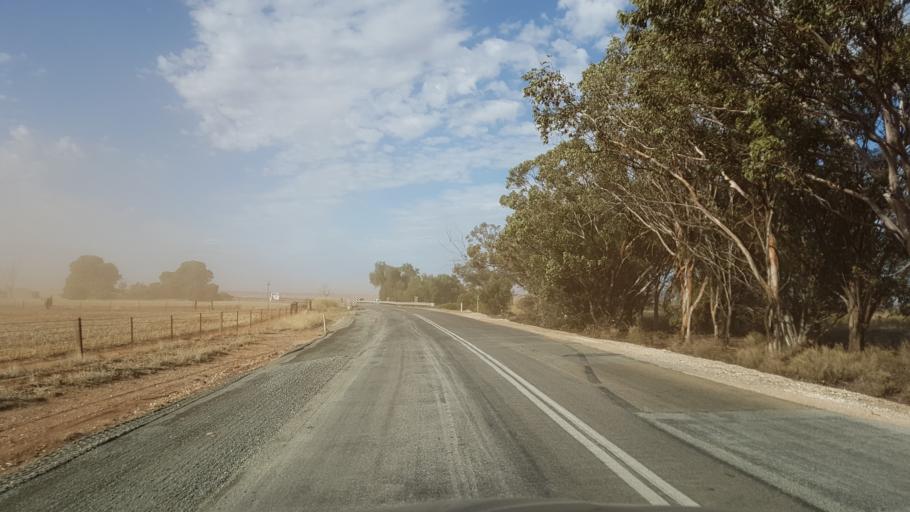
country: AU
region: South Australia
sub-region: Clare and Gilbert Valleys
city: Clare
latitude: -33.8785
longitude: 138.4793
